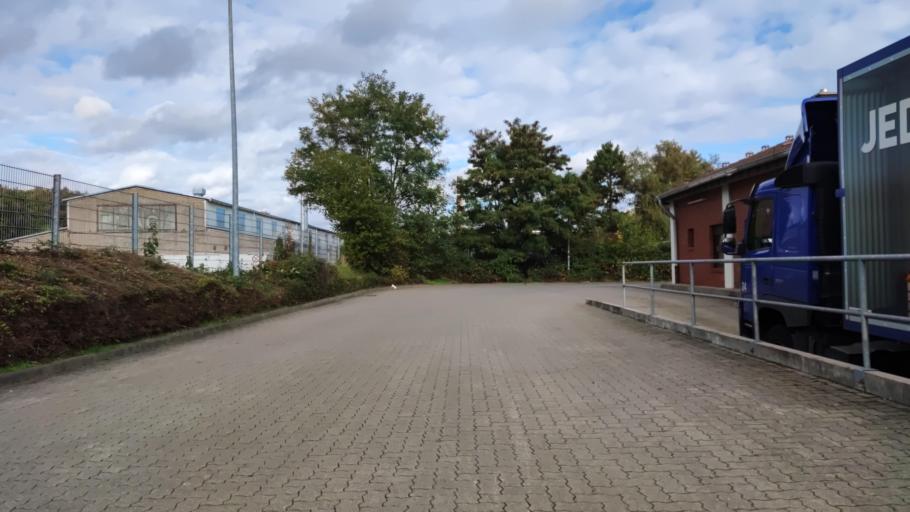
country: DE
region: North Rhine-Westphalia
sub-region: Regierungsbezirk Arnsberg
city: Herne
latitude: 51.5462
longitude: 7.2402
